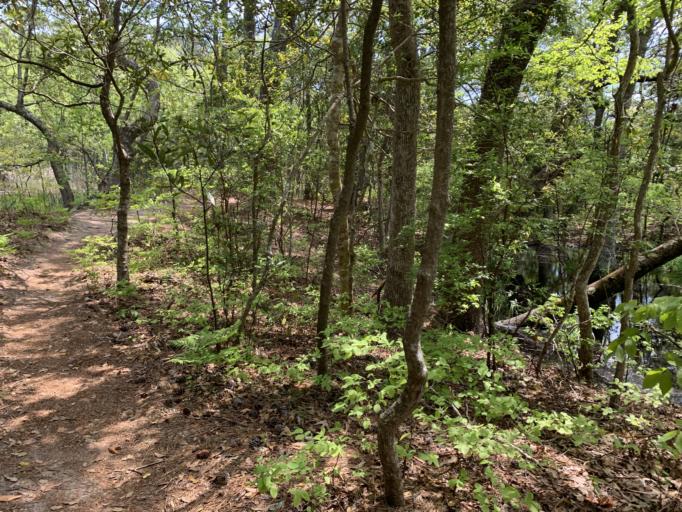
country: US
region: North Carolina
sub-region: Dare County
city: Nags Head
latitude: 35.9855
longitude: -75.6561
